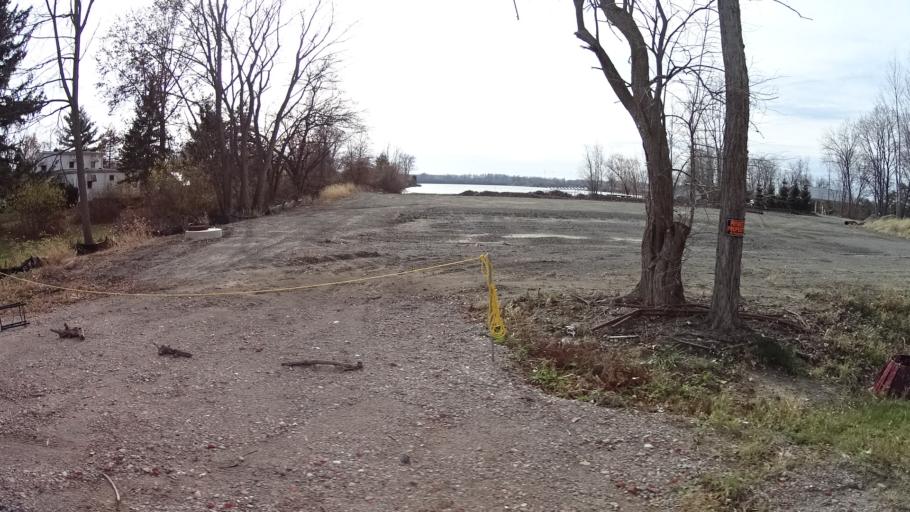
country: US
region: Ohio
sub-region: Lorain County
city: North Ridgeville
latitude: 41.3848
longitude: -81.9729
